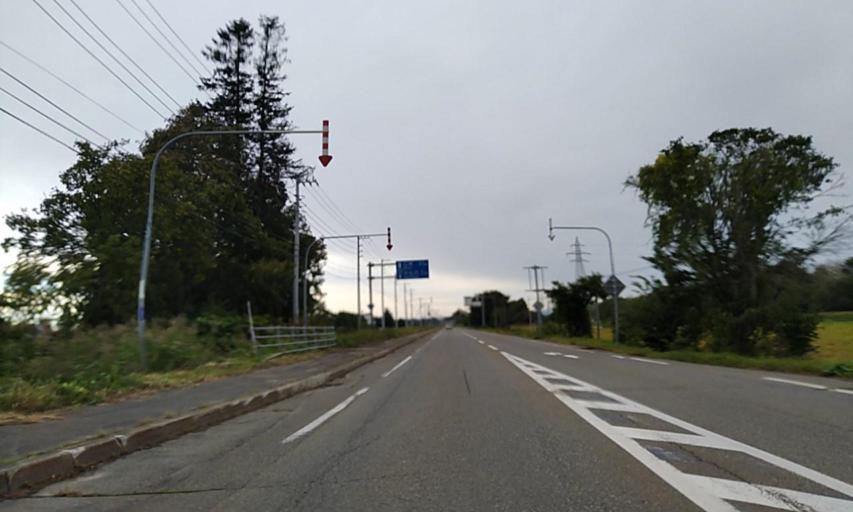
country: JP
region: Hokkaido
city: Obihiro
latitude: 42.7422
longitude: 143.1577
